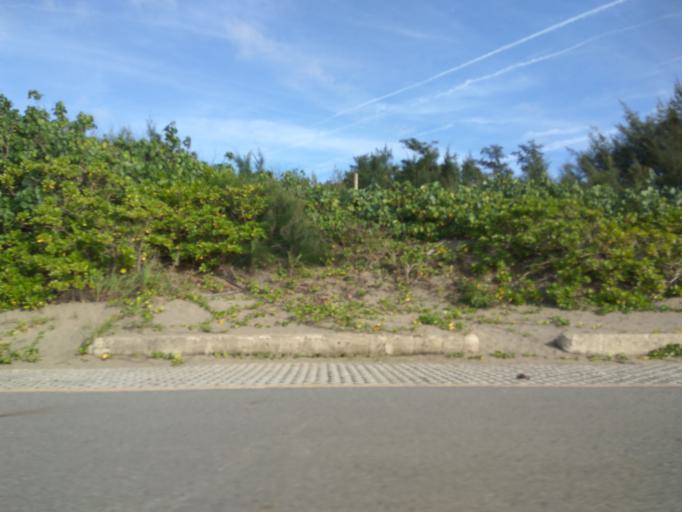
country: TW
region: Taiwan
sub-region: Hsinchu
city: Zhubei
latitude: 24.9839
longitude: 121.0161
